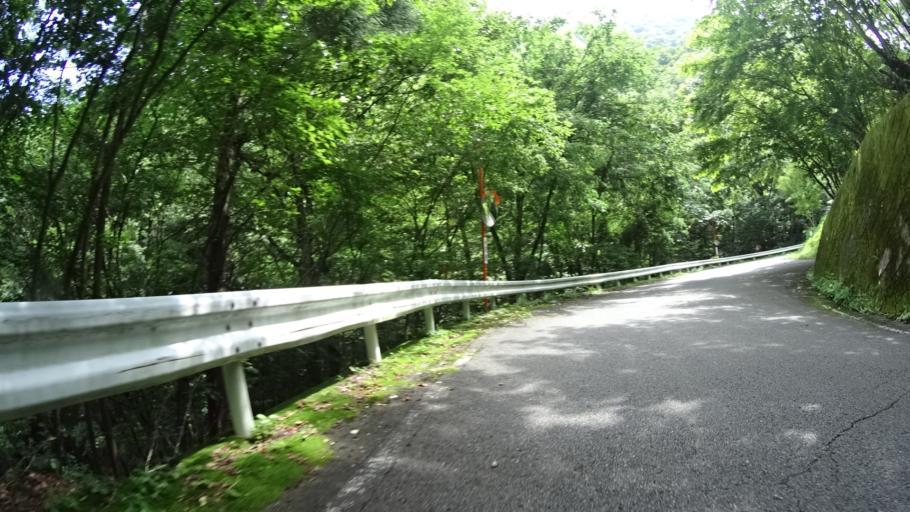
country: JP
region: Nagano
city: Saku
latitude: 36.0640
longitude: 138.6822
